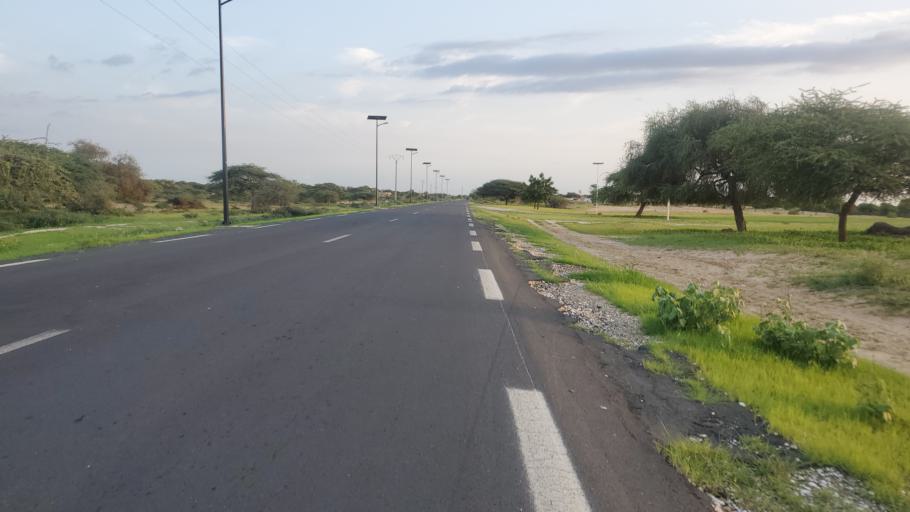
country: SN
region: Saint-Louis
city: Saint-Louis
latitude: 16.1468
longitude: -16.4097
